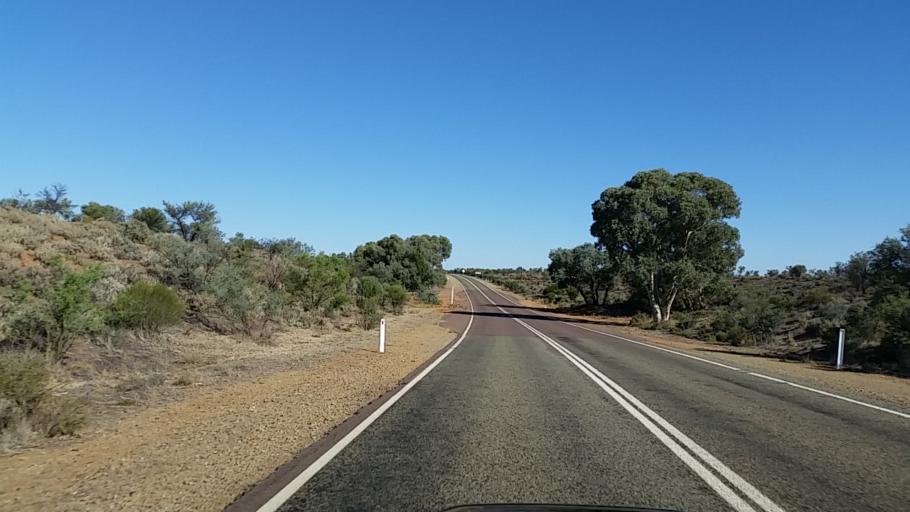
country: AU
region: South Australia
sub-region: Flinders Ranges
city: Quorn
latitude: -32.3743
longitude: 138.4995
